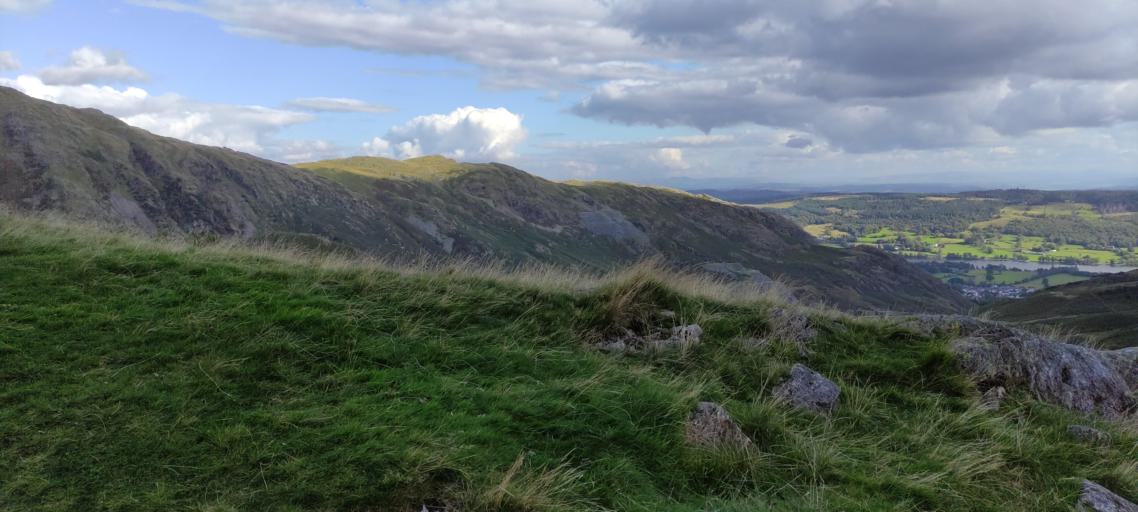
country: GB
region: England
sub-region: Cumbria
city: Ambleside
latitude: 54.3780
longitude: -3.1095
